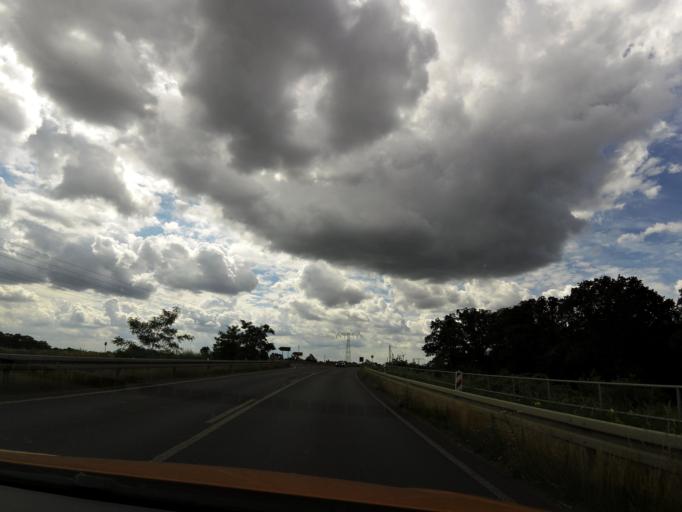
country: DE
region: Brandenburg
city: Grossbeeren
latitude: 52.3603
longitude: 13.2696
